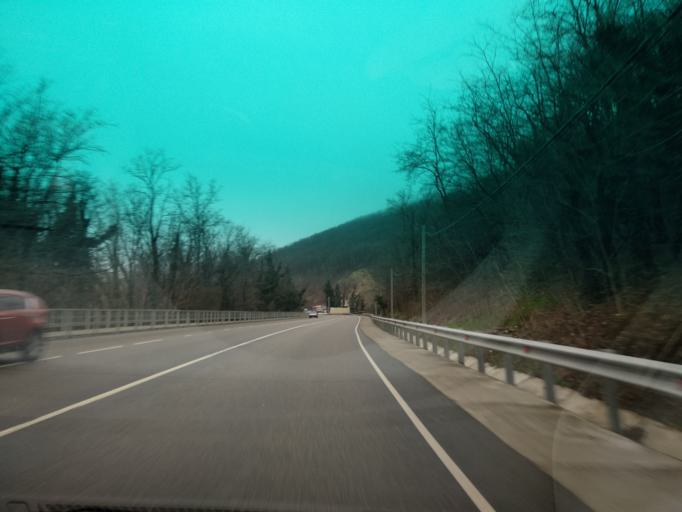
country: RU
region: Krasnodarskiy
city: Tuapse
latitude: 44.1078
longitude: 39.0741
